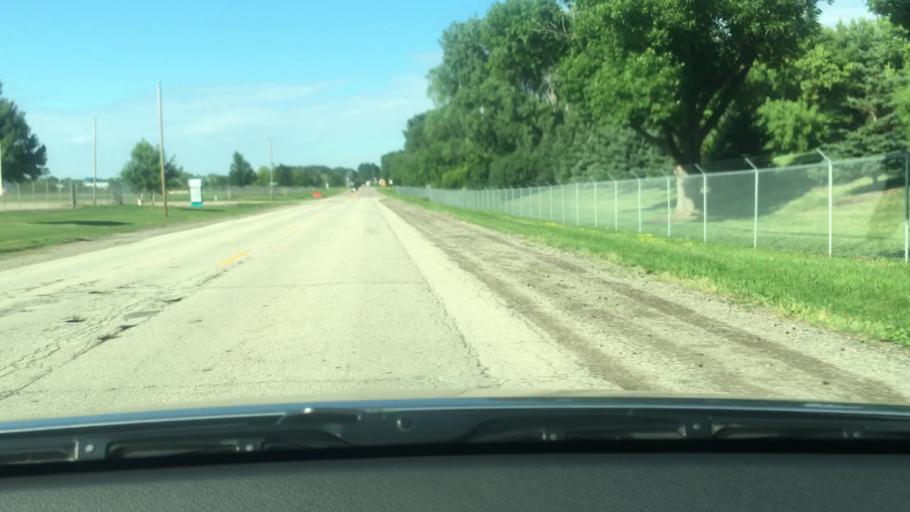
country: US
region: Wisconsin
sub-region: Winnebago County
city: Oshkosh
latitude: 43.9866
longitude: -88.5480
